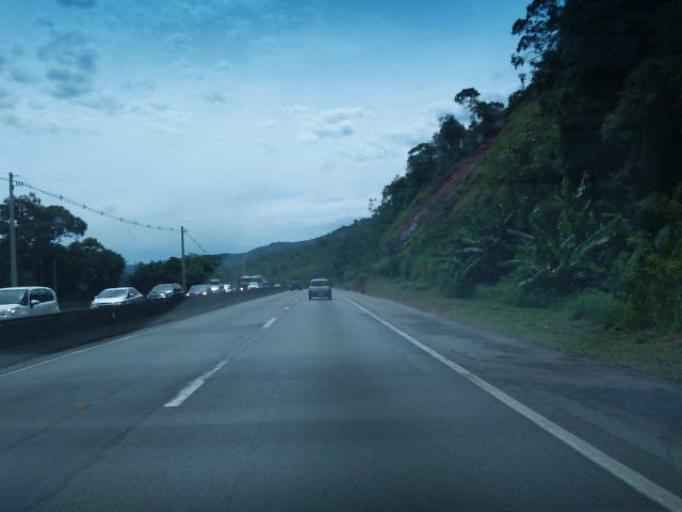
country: BR
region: Sao Paulo
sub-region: Miracatu
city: Miracatu
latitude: -24.1440
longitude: -47.2813
